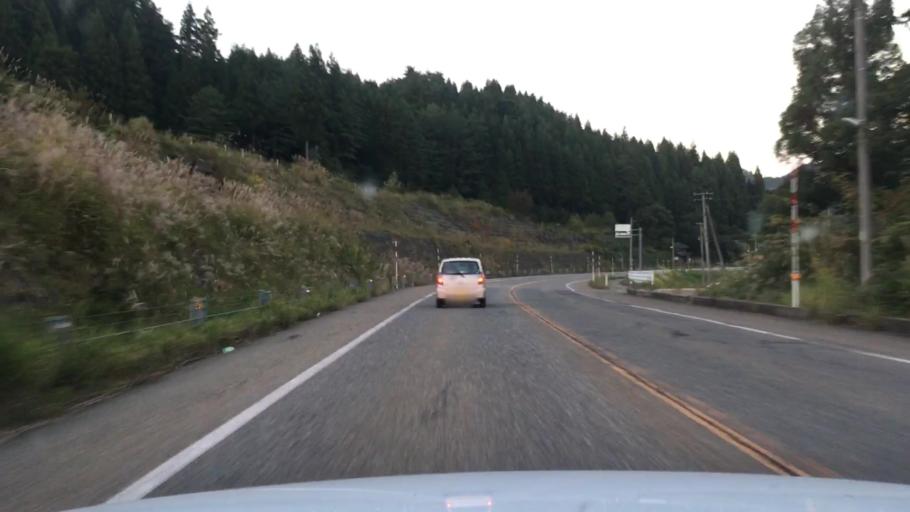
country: JP
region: Niigata
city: Murakami
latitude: 38.4336
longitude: 139.5880
